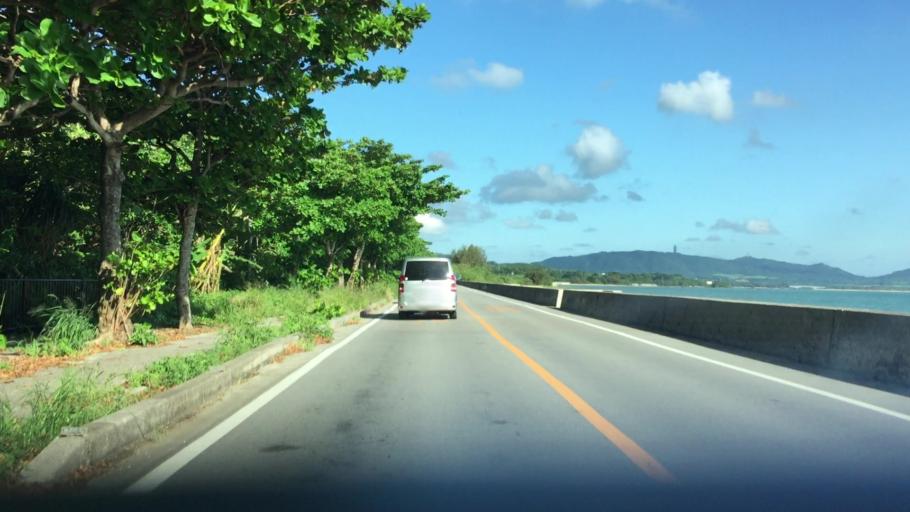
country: JP
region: Okinawa
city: Ishigaki
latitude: 24.4277
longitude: 124.1254
